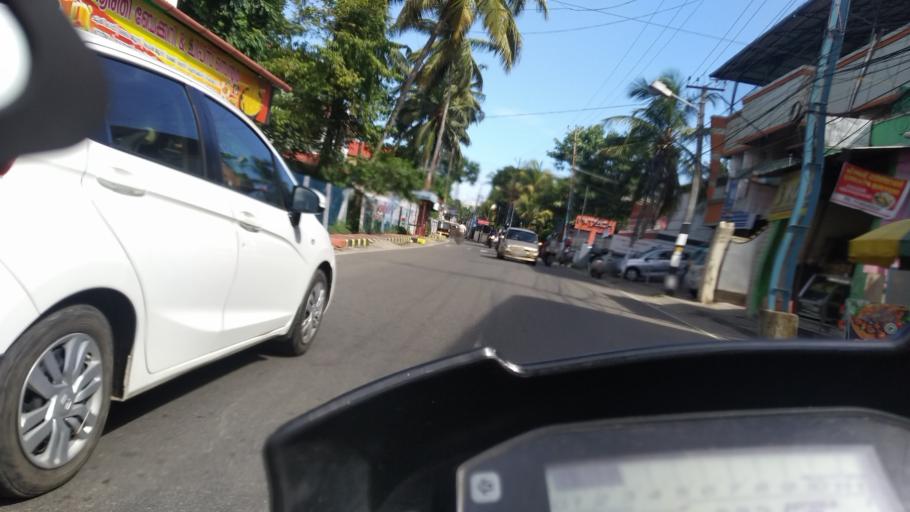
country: IN
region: Kerala
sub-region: Ernakulam
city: Elur
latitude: 10.0213
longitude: 76.2741
